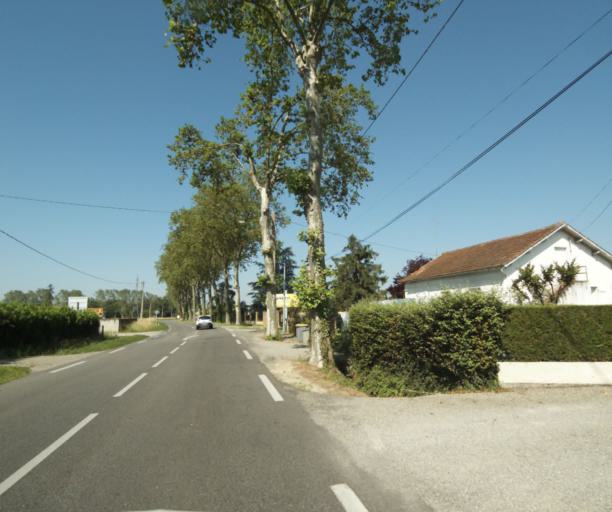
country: FR
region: Midi-Pyrenees
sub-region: Departement du Tarn-et-Garonne
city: Montbeton
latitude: 43.9995
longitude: 1.3240
